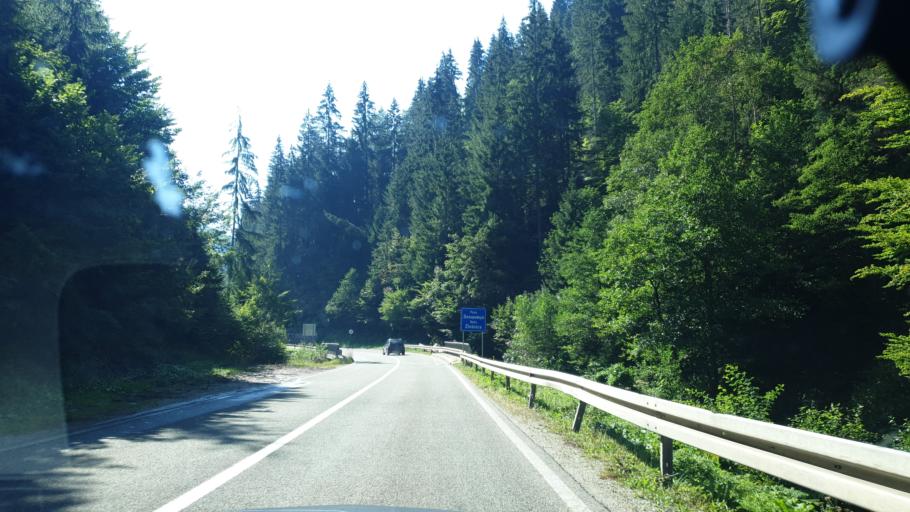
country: RS
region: Central Serbia
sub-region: Zlatiborski Okrug
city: Nova Varos
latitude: 43.4805
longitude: 19.8300
